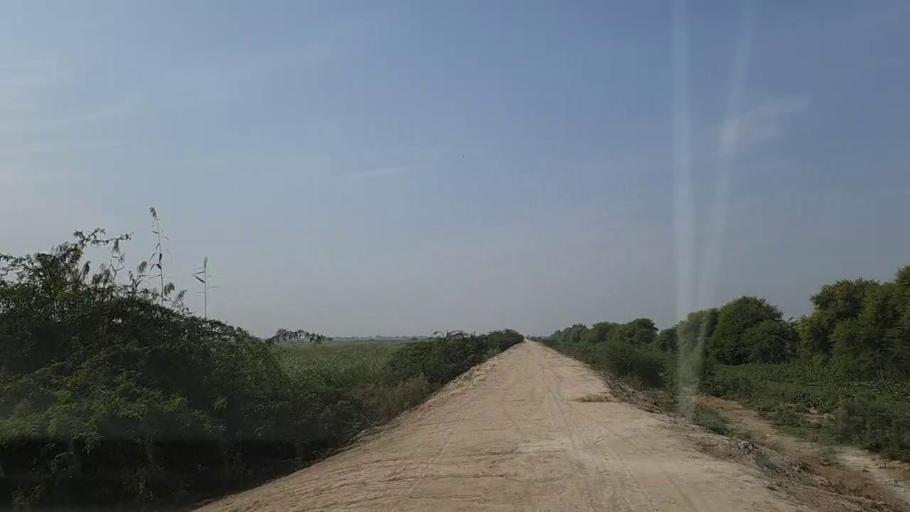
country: PK
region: Sindh
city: Mirpur Batoro
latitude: 24.6537
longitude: 68.2419
